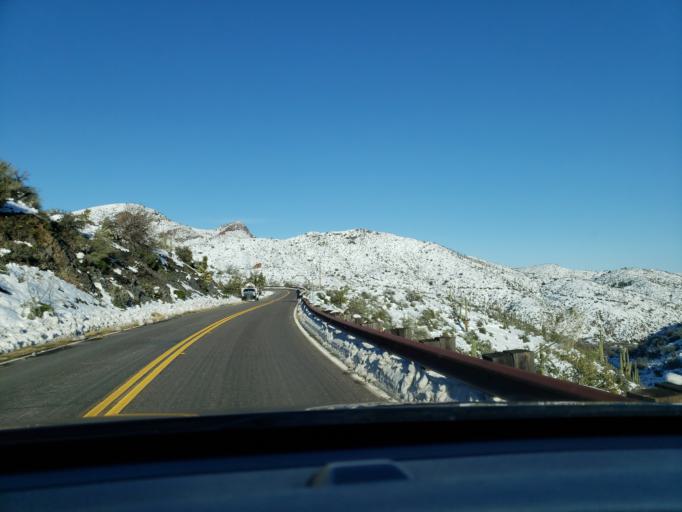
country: US
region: Arizona
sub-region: Maricopa County
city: Carefree
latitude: 33.8937
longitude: -111.8198
